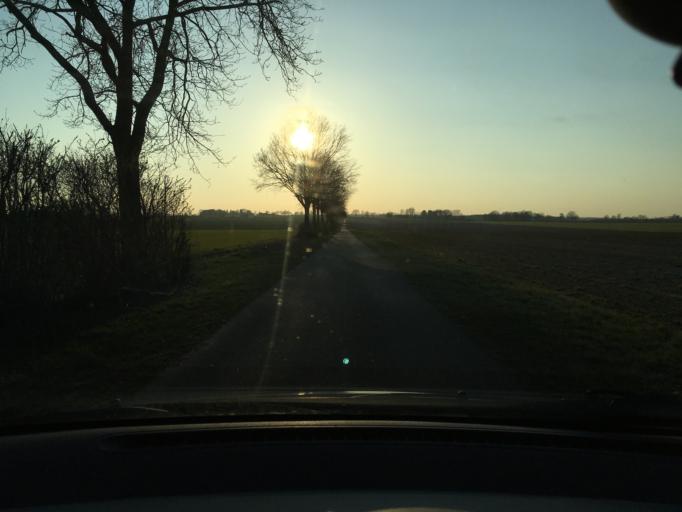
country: DE
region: Lower Saxony
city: Romstedt
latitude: 53.1486
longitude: 10.6563
